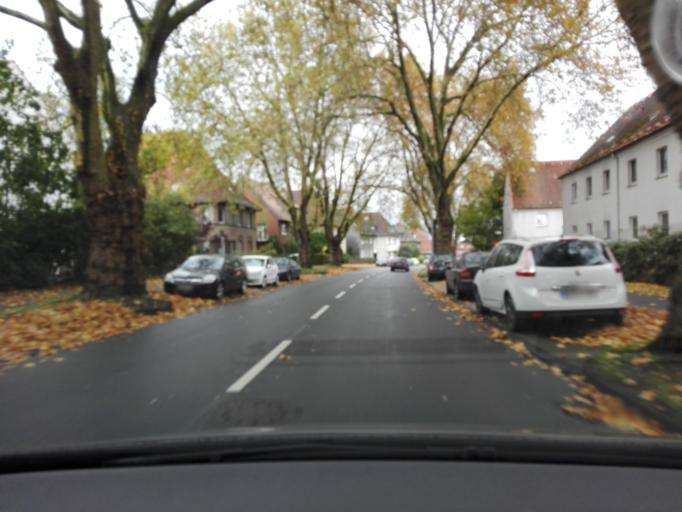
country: DE
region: North Rhine-Westphalia
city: Lunen
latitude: 51.6215
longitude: 7.5165
